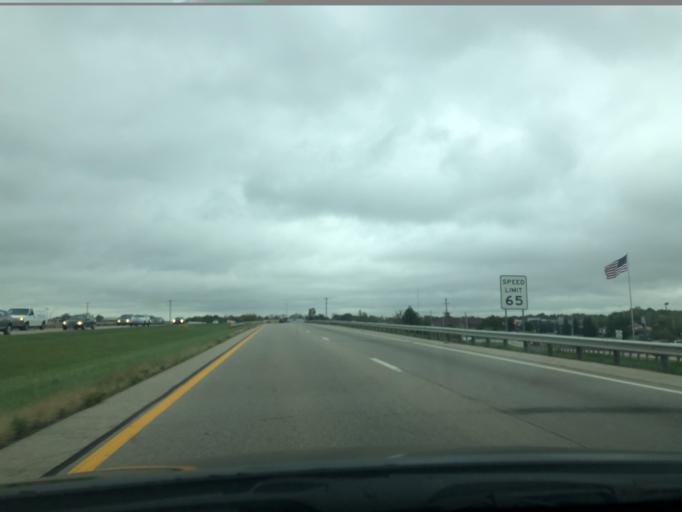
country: US
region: Ohio
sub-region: Union County
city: Marysville
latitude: 40.2370
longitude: -83.3436
